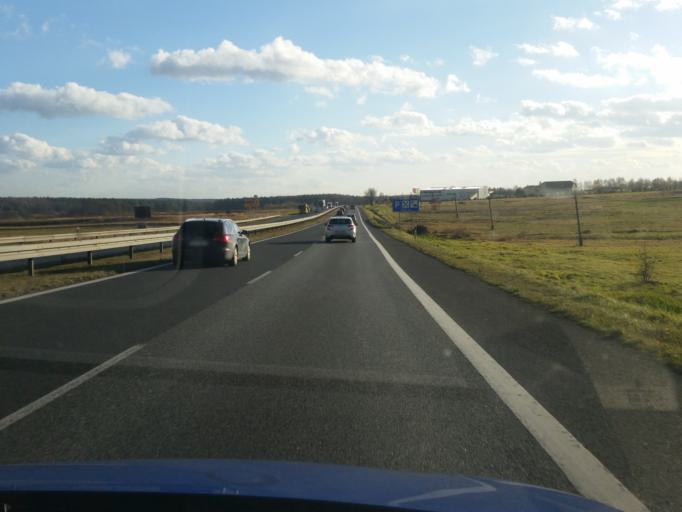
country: PL
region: Silesian Voivodeship
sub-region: Powiat myszkowski
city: Kozieglowy
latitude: 50.5594
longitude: 19.1758
